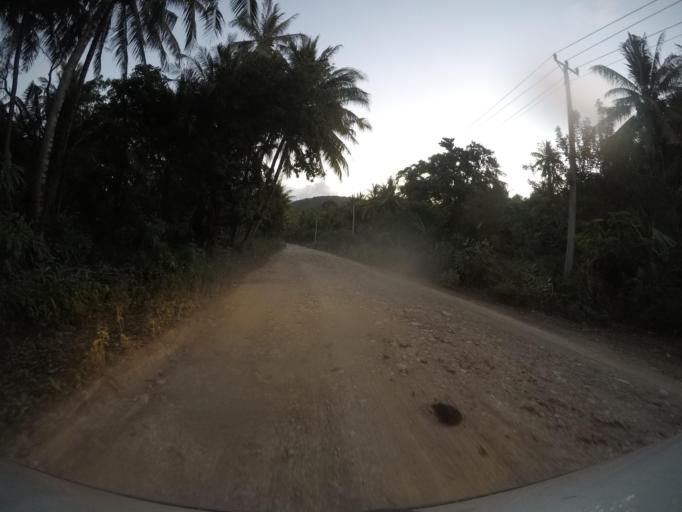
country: TL
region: Viqueque
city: Viqueque
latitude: -8.7882
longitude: 126.6306
